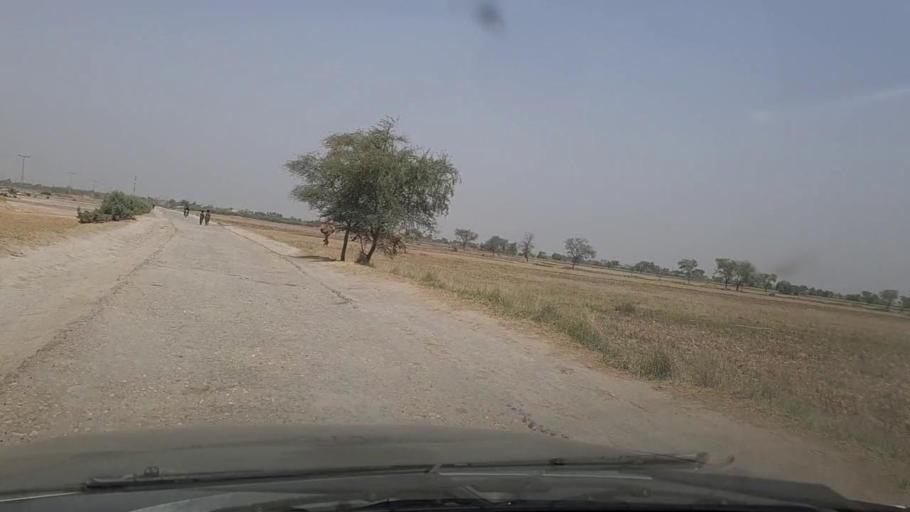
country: PK
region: Balochistan
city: Sohbatpur
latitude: 28.4188
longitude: 68.6831
